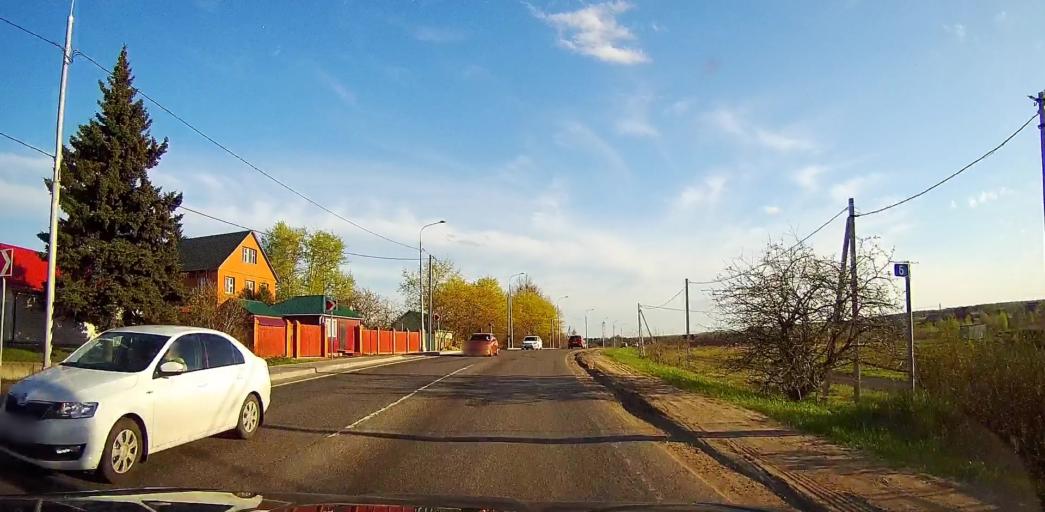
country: RU
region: Moskovskaya
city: Bronnitsy
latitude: 55.3381
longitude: 38.2220
